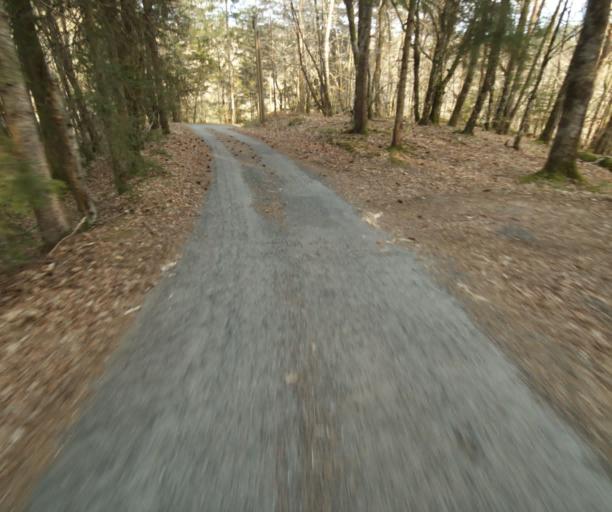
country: FR
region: Limousin
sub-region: Departement de la Correze
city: Correze
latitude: 45.3600
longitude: 1.8318
